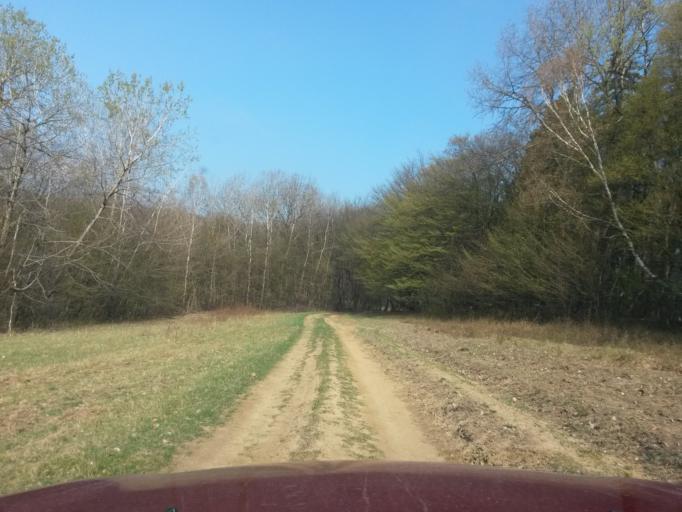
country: SK
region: Presovsky
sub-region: Okres Presov
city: Presov
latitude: 48.9237
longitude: 21.1650
